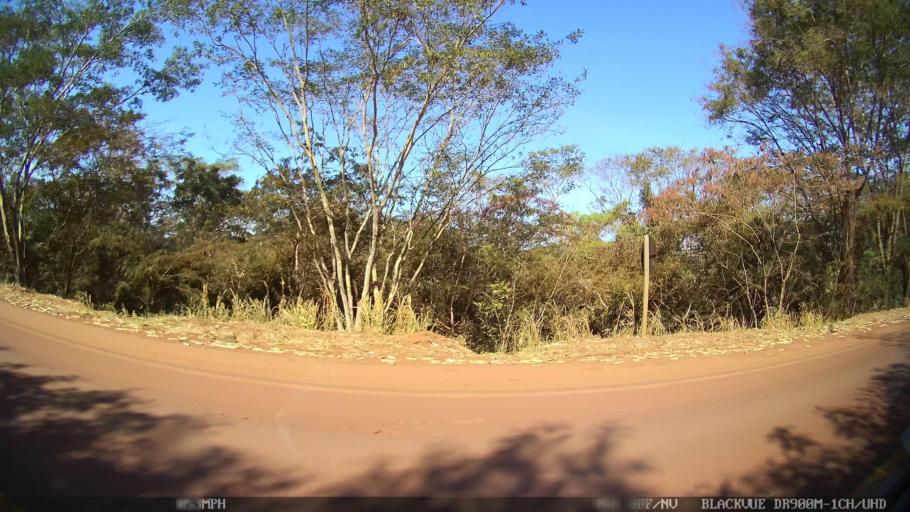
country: BR
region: Sao Paulo
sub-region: Barretos
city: Barretos
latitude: -20.4562
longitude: -48.4607
